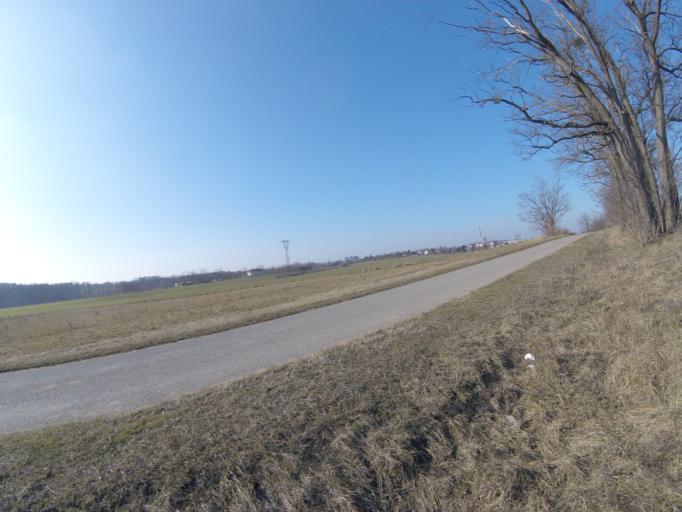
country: HU
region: Komarom-Esztergom
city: Oroszlany
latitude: 47.4757
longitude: 18.3317
